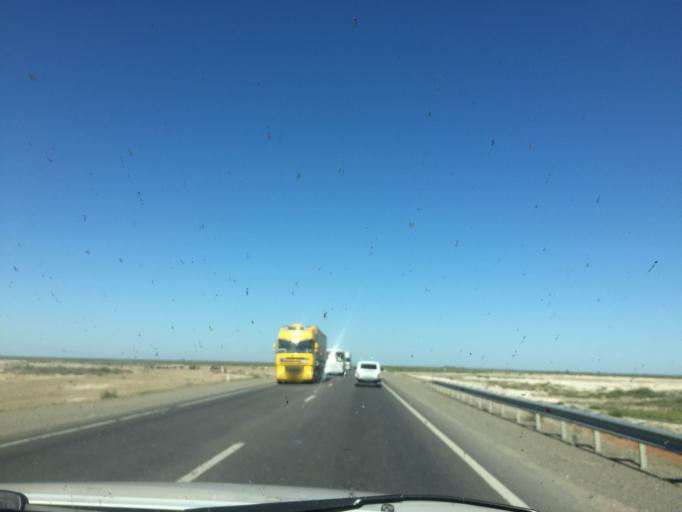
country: KZ
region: Qyzylorda
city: Kyzyl-Orda
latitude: 44.8851
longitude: 65.2635
